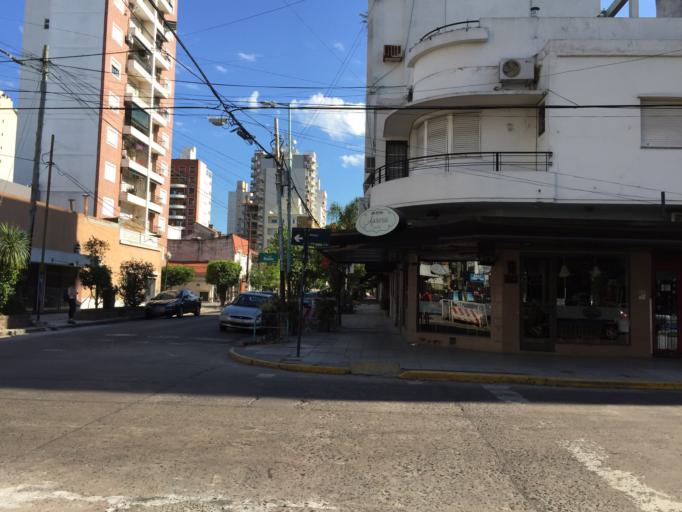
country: AR
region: Buenos Aires
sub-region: Partido de Lomas de Zamora
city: Lomas de Zamora
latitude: -34.7433
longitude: -58.3917
